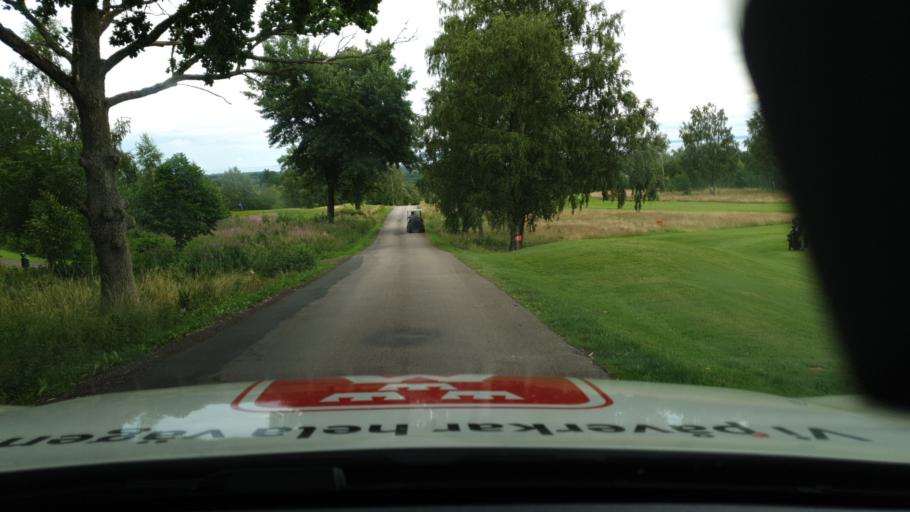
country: SE
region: Vaestra Goetaland
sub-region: Hjo Kommun
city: Hjo
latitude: 58.2511
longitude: 14.2127
